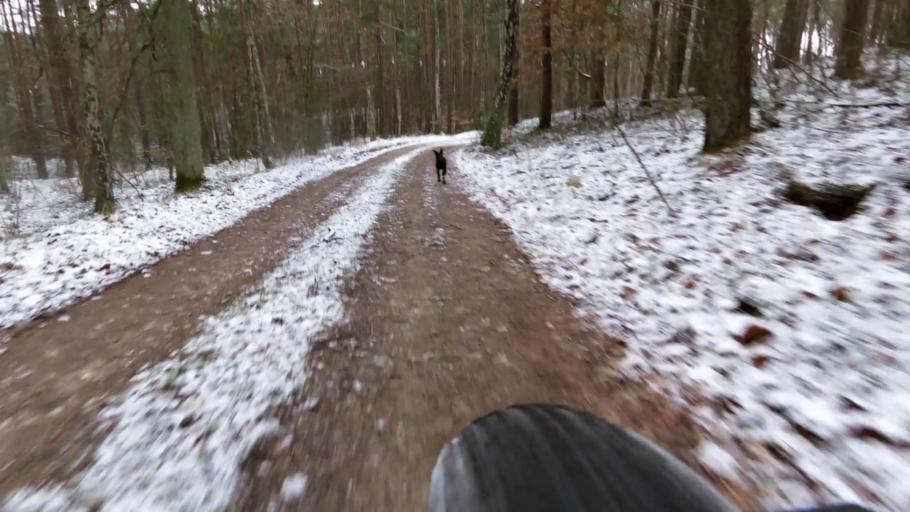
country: PL
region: West Pomeranian Voivodeship
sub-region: Powiat walecki
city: Miroslawiec
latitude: 53.3305
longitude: 16.1024
